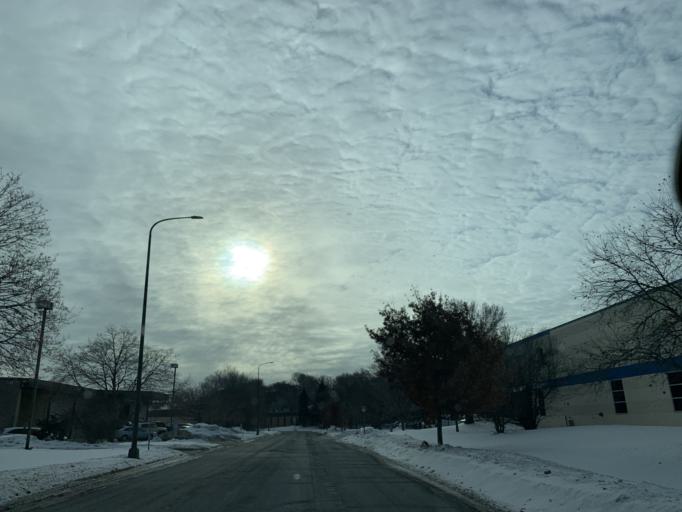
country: US
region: Minnesota
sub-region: Ramsey County
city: Saint Paul
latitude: 44.9371
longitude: -93.0793
